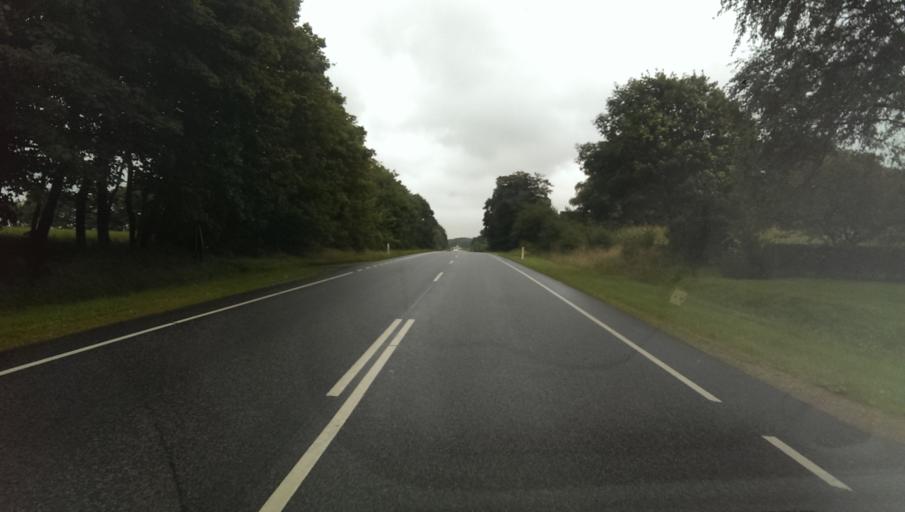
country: DK
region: South Denmark
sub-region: Esbjerg Kommune
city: Tjaereborg
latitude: 55.4926
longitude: 8.6277
